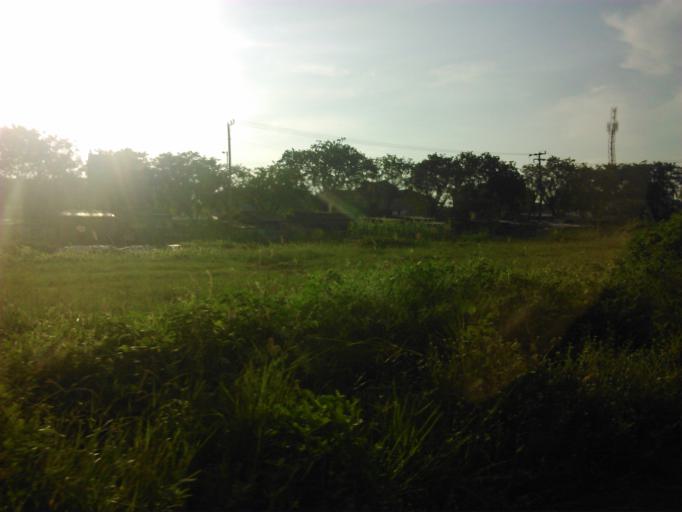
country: ID
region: East Java
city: Wonorejo
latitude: -7.2908
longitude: 112.8025
